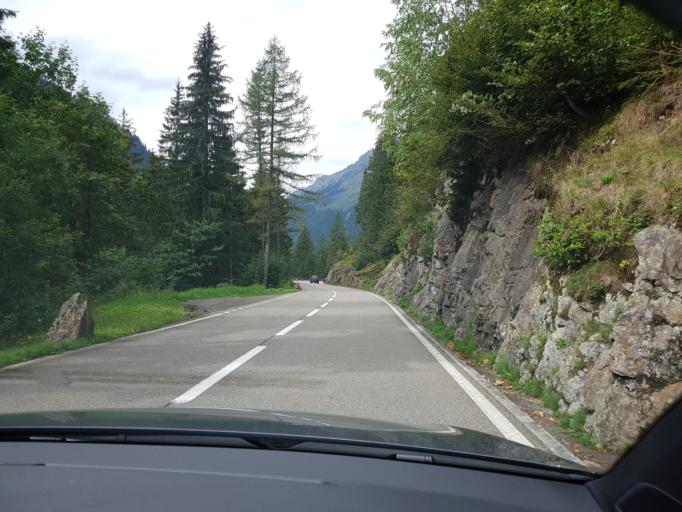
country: CH
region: Obwalden
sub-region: Obwalden
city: Engelberg
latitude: 46.7372
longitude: 8.3800
